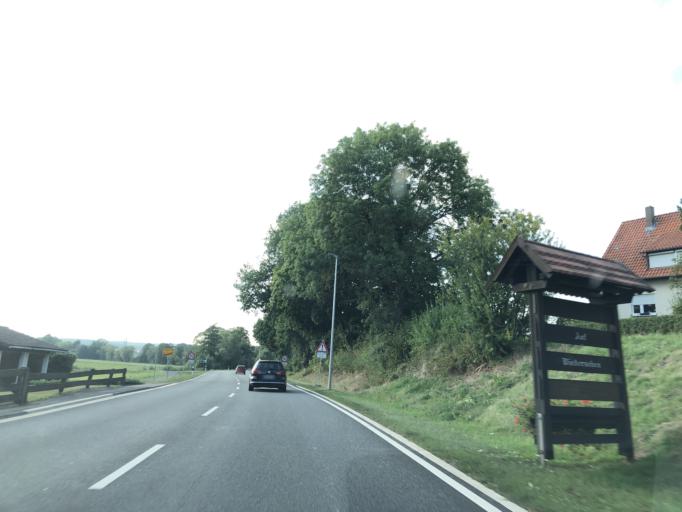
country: DE
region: Hesse
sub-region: Regierungsbezirk Giessen
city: Munchhausen
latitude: 50.9653
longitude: 8.7146
